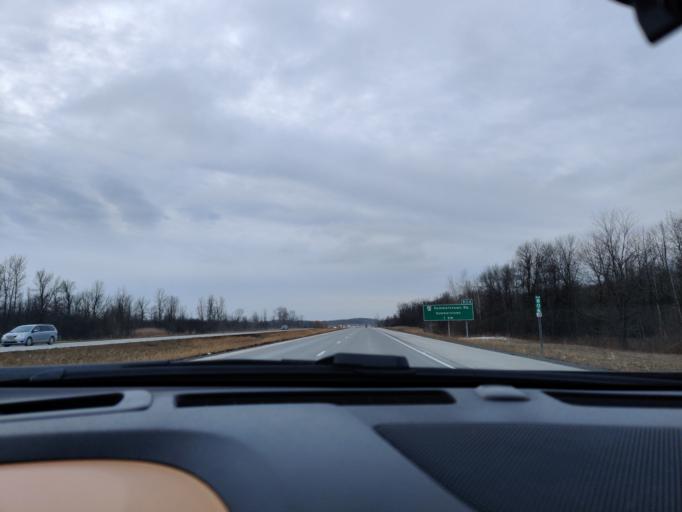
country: CA
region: Ontario
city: Cornwall
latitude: 45.0982
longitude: -74.5780
